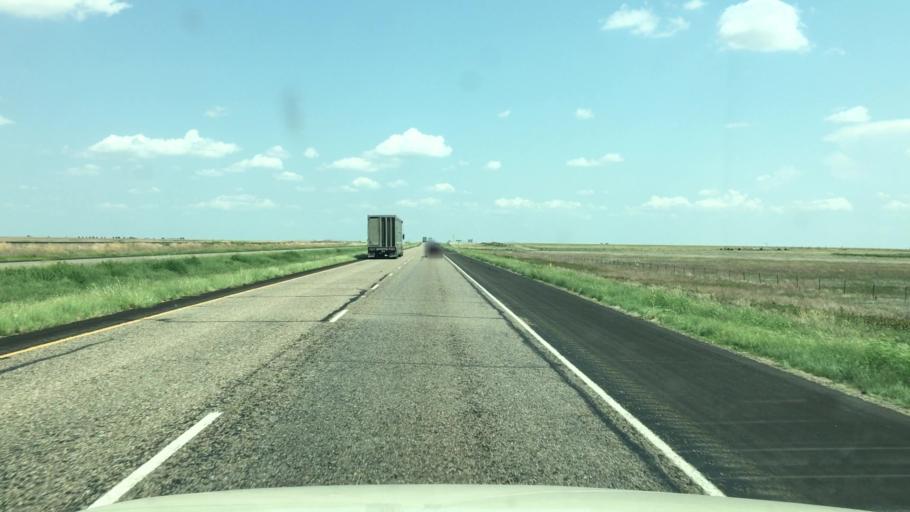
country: US
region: Texas
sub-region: Armstrong County
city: Claude
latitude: 35.1325
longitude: -101.4210
